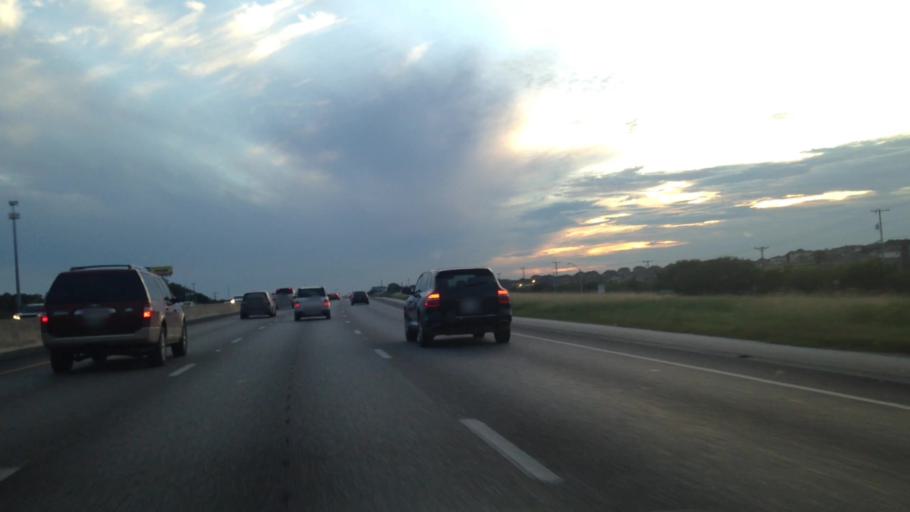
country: US
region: Texas
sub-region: Guadalupe County
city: Northcliff
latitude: 29.6549
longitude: -98.1867
